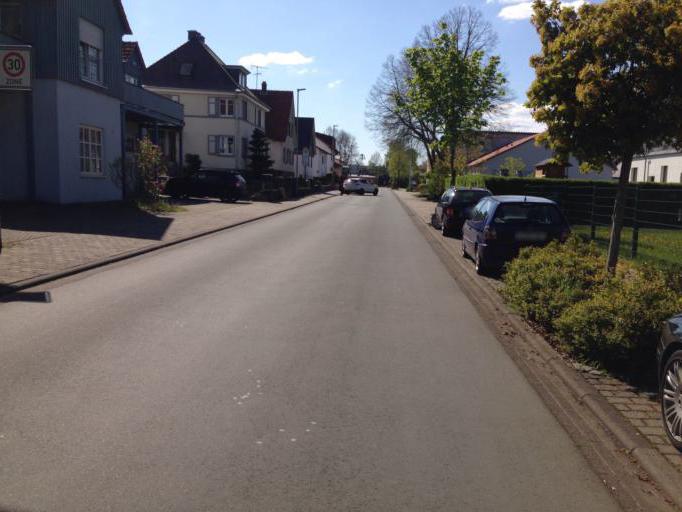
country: DE
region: Hesse
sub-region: Regierungsbezirk Giessen
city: Grunberg
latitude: 50.5582
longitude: 8.9058
